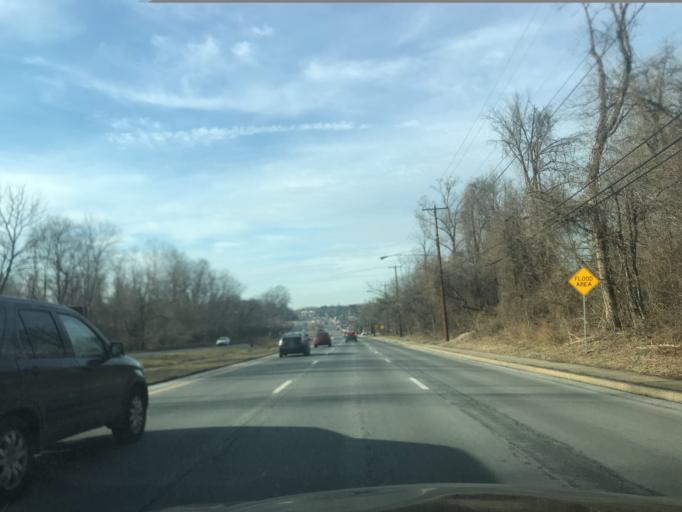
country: US
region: Maryland
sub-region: Montgomery County
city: Aspen Hill
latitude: 39.0757
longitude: -77.0684
